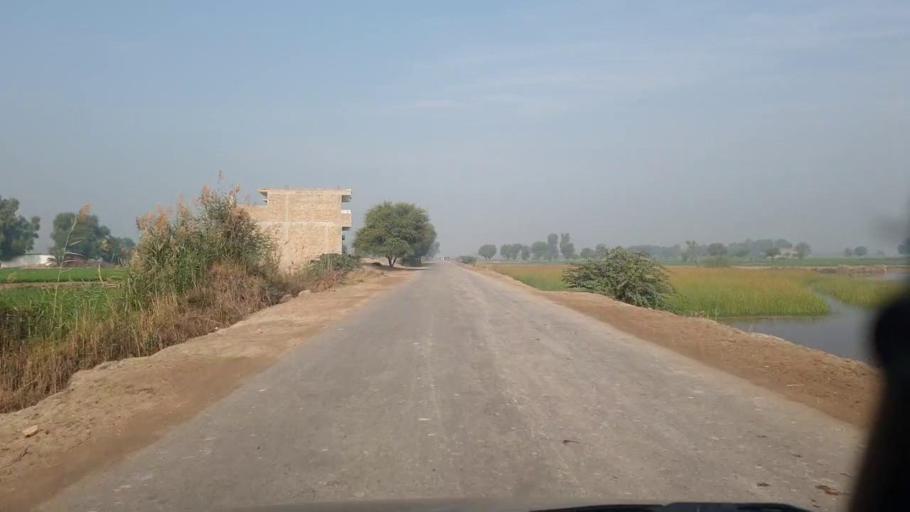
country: PK
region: Sindh
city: Shahdadpur
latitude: 25.9392
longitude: 68.6034
